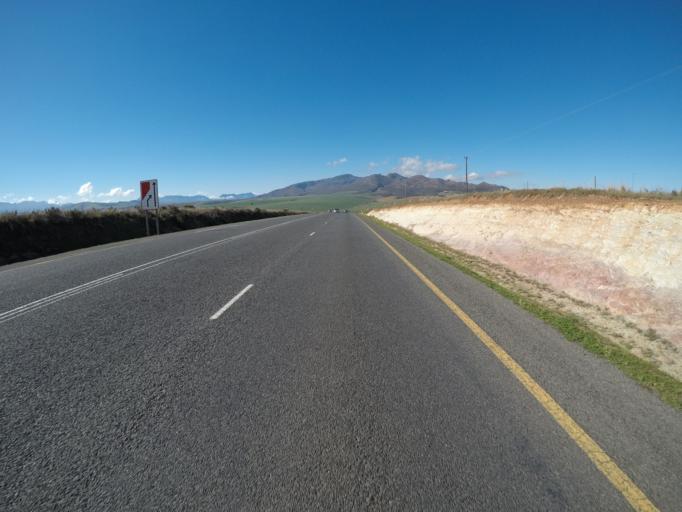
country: ZA
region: Western Cape
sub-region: Overberg District Municipality
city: Caledon
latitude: -34.2097
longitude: 19.3840
